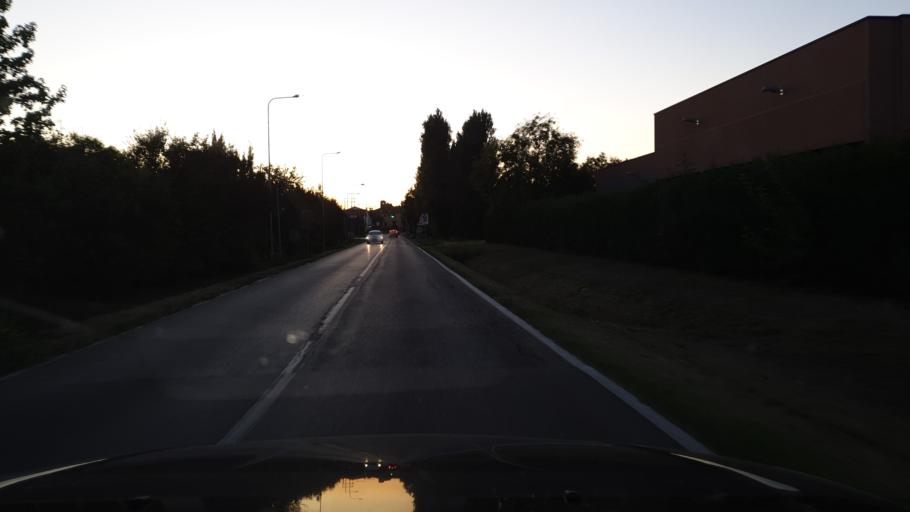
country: IT
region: Emilia-Romagna
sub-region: Provincia di Bologna
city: Altedo
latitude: 44.6615
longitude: 11.4906
